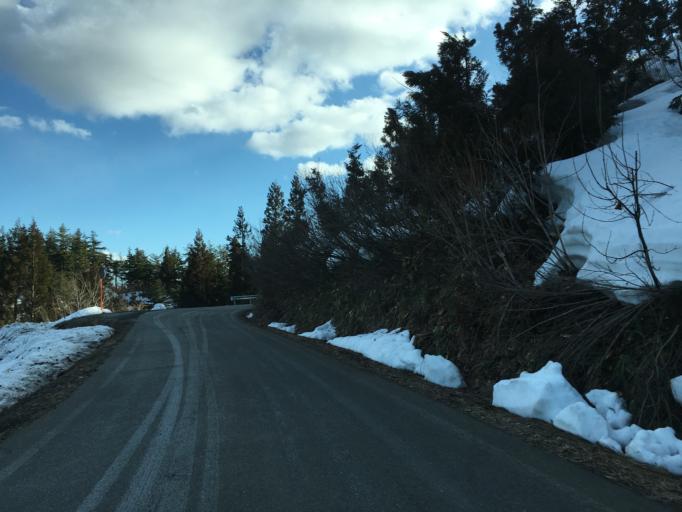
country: JP
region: Yamagata
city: Yonezawa
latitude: 37.9251
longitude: 139.9431
